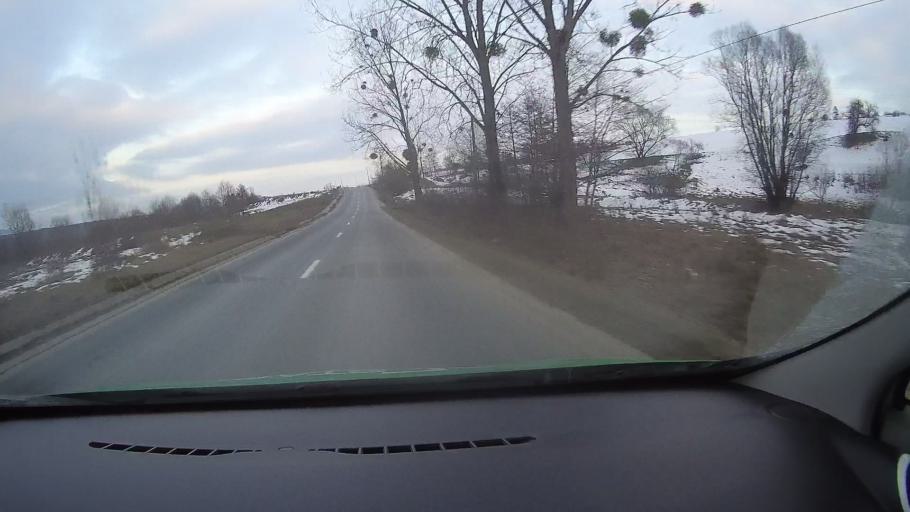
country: RO
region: Harghita
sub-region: Comuna Lupeni
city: Lupeni
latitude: 46.3574
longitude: 25.1999
